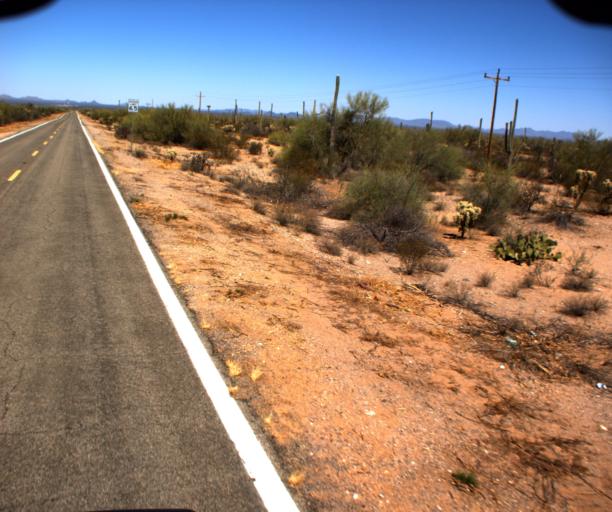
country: US
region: Arizona
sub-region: Pima County
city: Sells
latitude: 32.1822
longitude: -112.2861
